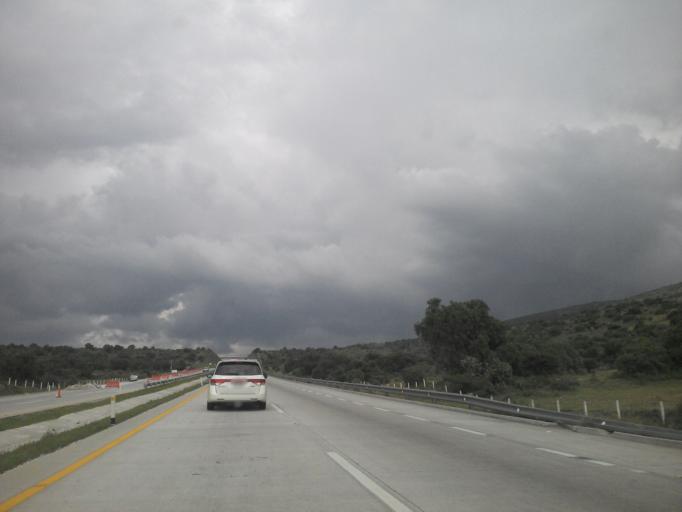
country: MX
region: Mexico
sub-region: Hueypoxtla
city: Santa Maria Ajoloapan
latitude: 19.9604
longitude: -99.0315
